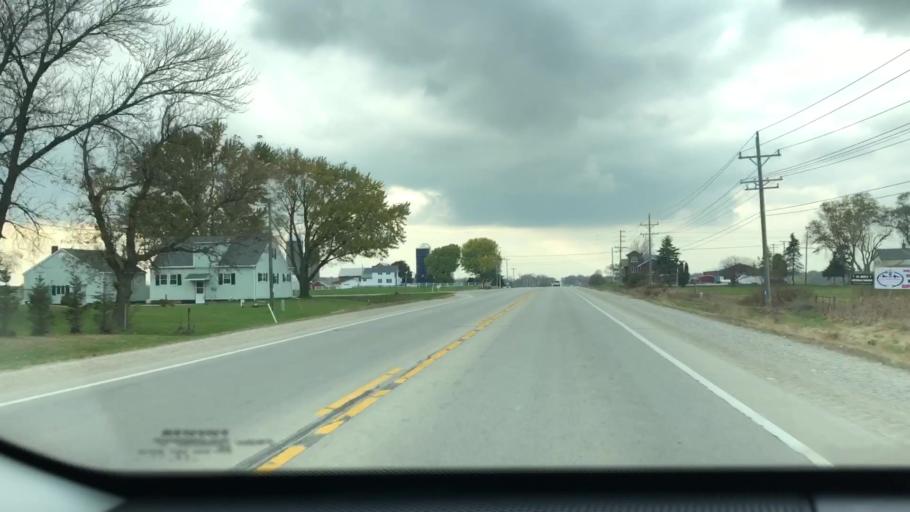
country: US
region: Wisconsin
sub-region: Outagamie County
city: Seymour
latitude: 44.5004
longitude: -88.3077
